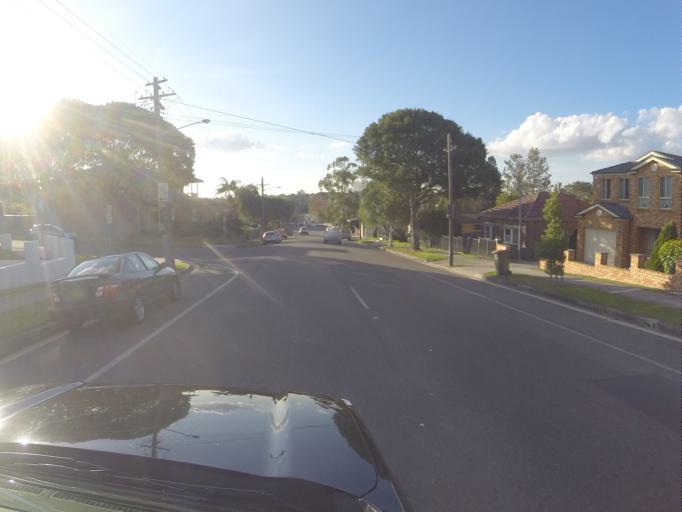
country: AU
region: New South Wales
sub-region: Rockdale
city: Bexley North
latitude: -33.9412
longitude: 151.1145
